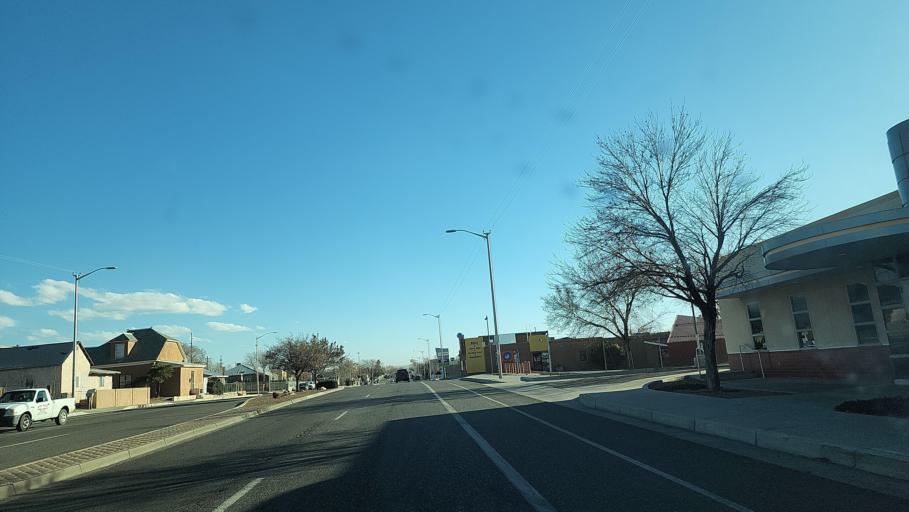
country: US
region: New Mexico
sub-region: Bernalillo County
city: Albuquerque
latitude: 35.0686
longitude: -106.6456
